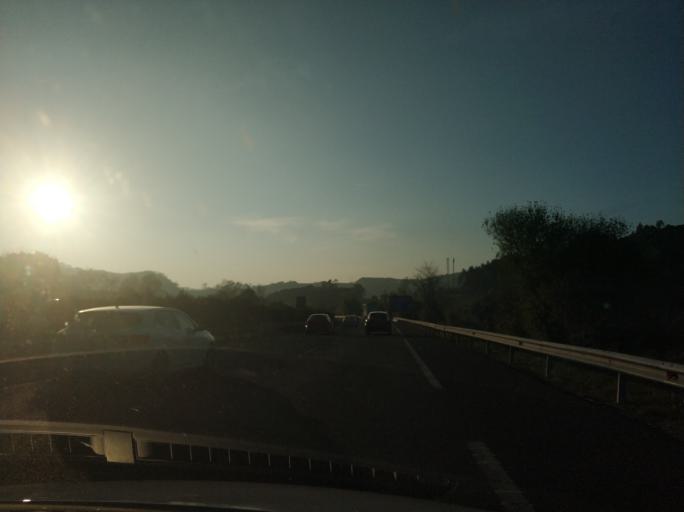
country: ES
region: Cantabria
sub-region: Provincia de Cantabria
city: Barcena de Cicero
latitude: 43.4124
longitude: -3.5308
